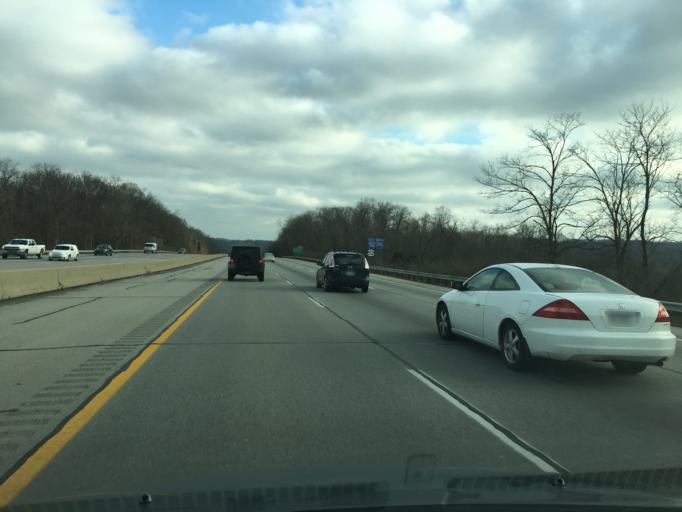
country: US
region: Ohio
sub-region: Hamilton County
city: Grandview
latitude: 39.2121
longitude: -84.7225
